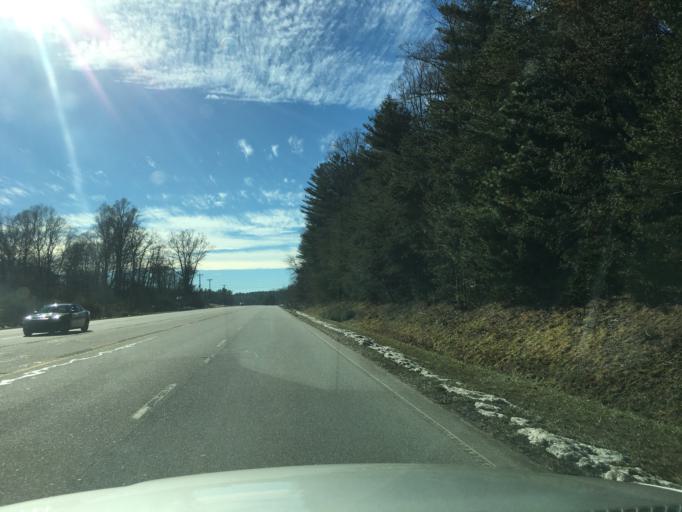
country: US
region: North Carolina
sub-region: Henderson County
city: Mills River
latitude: 35.3612
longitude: -82.5984
